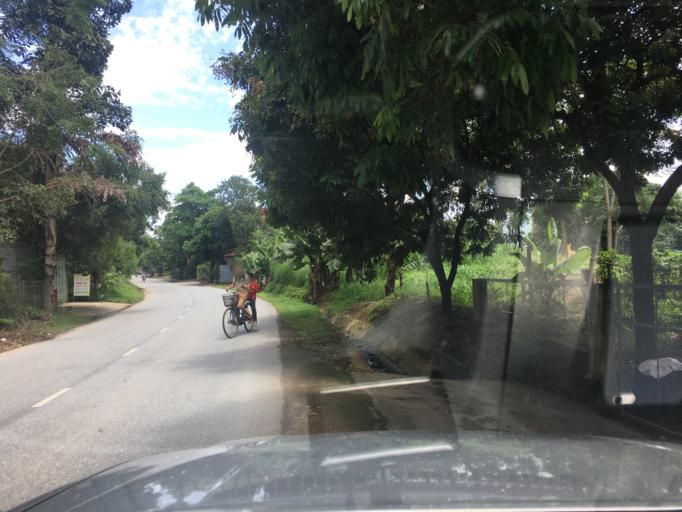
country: VN
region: Yen Bai
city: Son Thinh
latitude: 21.6527
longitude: 104.5008
